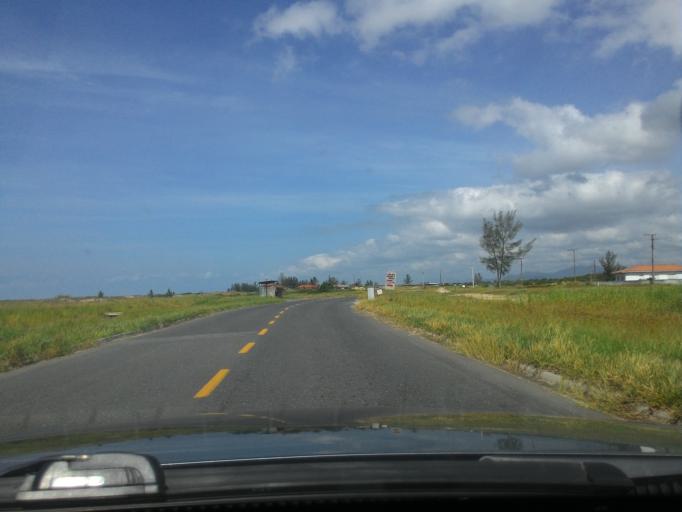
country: BR
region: Sao Paulo
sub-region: Iguape
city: Iguape
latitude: -24.8031
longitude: -47.6332
